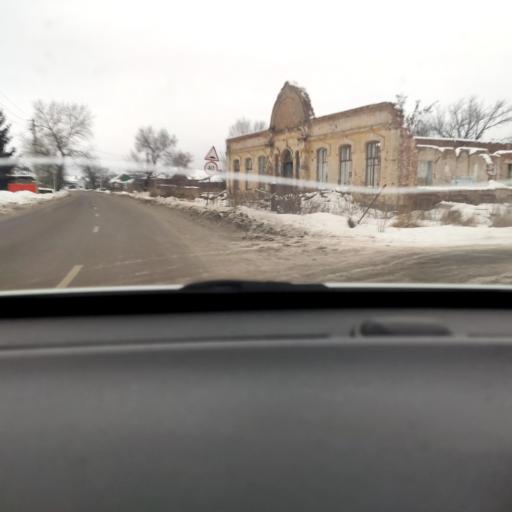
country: RU
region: Voronezj
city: Somovo
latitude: 51.7474
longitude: 39.3382
